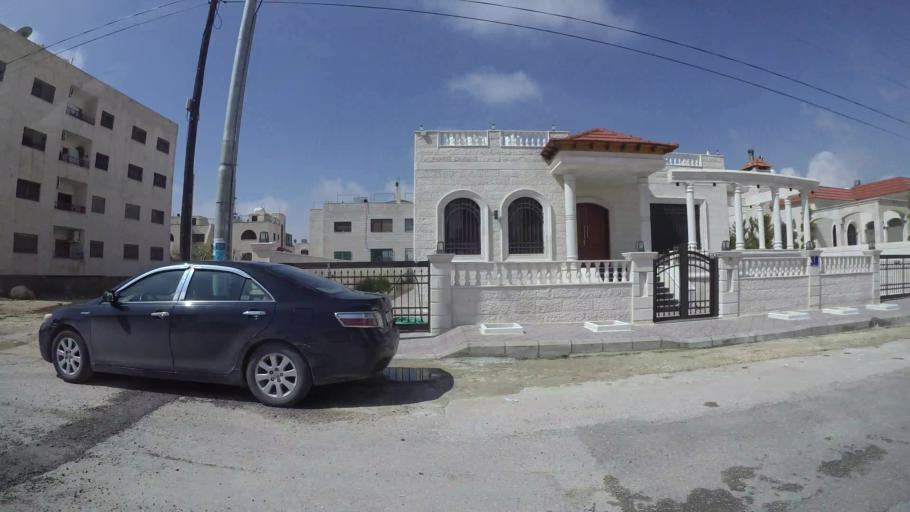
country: JO
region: Amman
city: Al Bunayyat ash Shamaliyah
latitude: 31.8996
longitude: 35.8898
